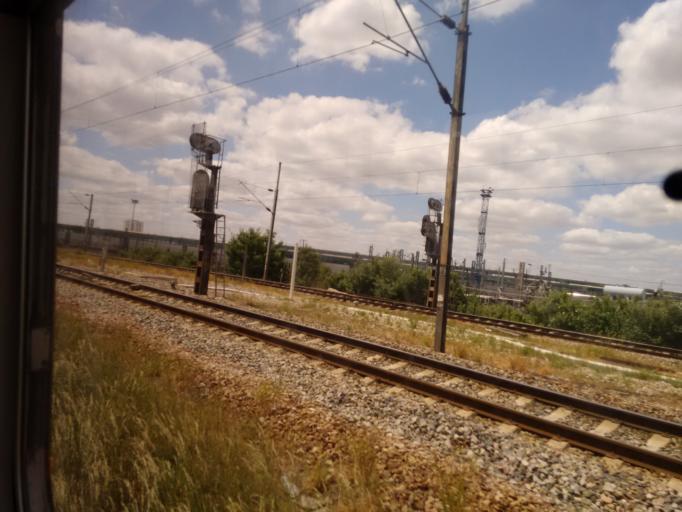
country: FR
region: Ile-de-France
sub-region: Paris
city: Saint-Ouen
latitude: 48.9130
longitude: 2.3536
